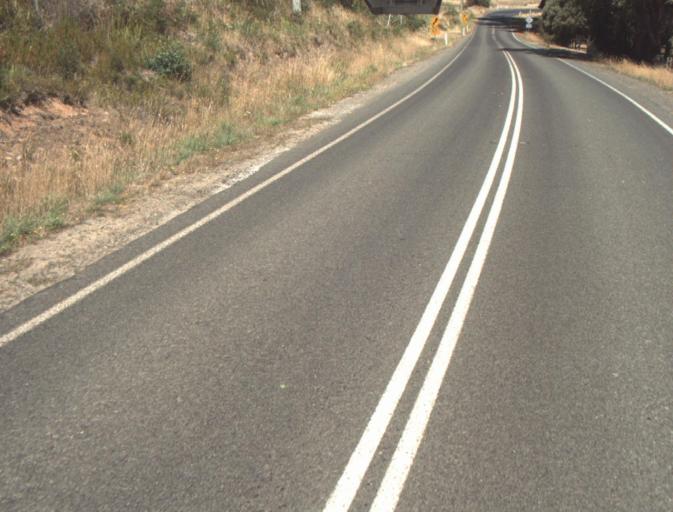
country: AU
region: Tasmania
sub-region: Launceston
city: Newstead
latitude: -41.3255
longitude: 147.3571
